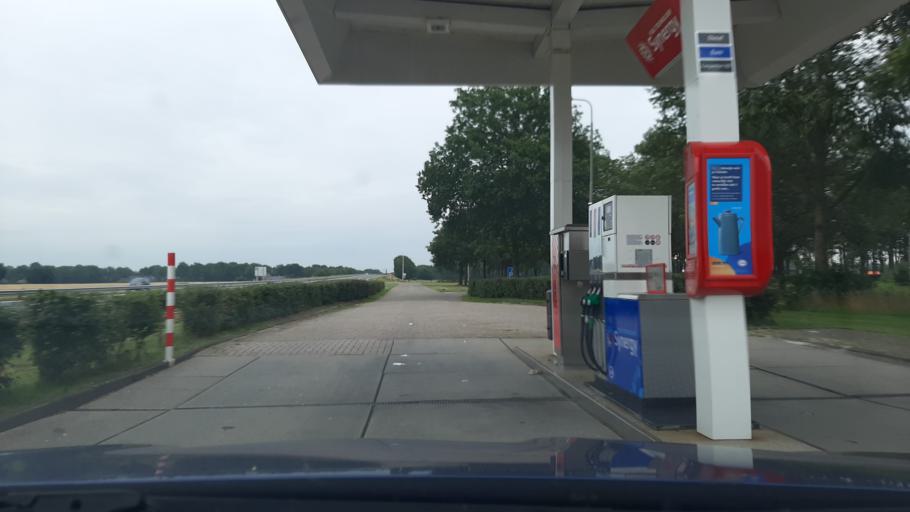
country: NL
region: Drenthe
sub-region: Gemeente Assen
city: Assen
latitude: 52.9704
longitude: 6.6166
